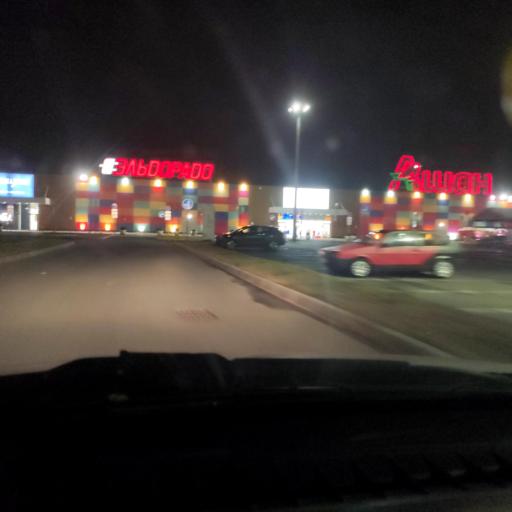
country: RU
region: Samara
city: Tol'yatti
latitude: 53.5509
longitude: 49.3432
